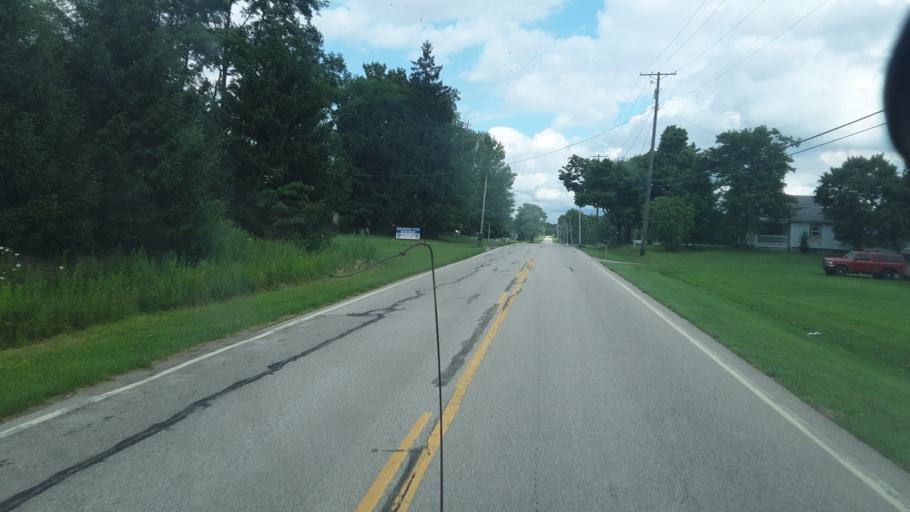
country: US
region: Ohio
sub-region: Ashtabula County
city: Jefferson
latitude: 41.7817
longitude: -80.7955
